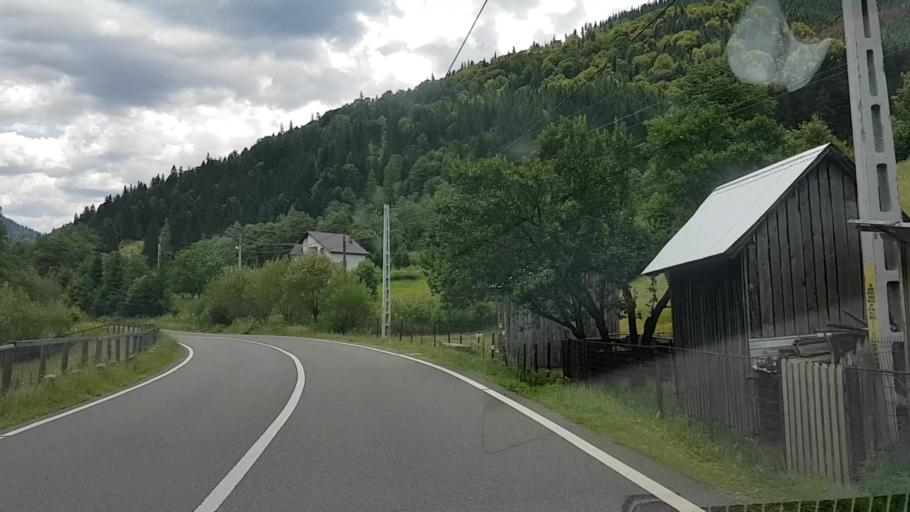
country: RO
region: Suceava
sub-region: Comuna Crucea
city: Crucea
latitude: 47.3291
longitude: 25.6201
